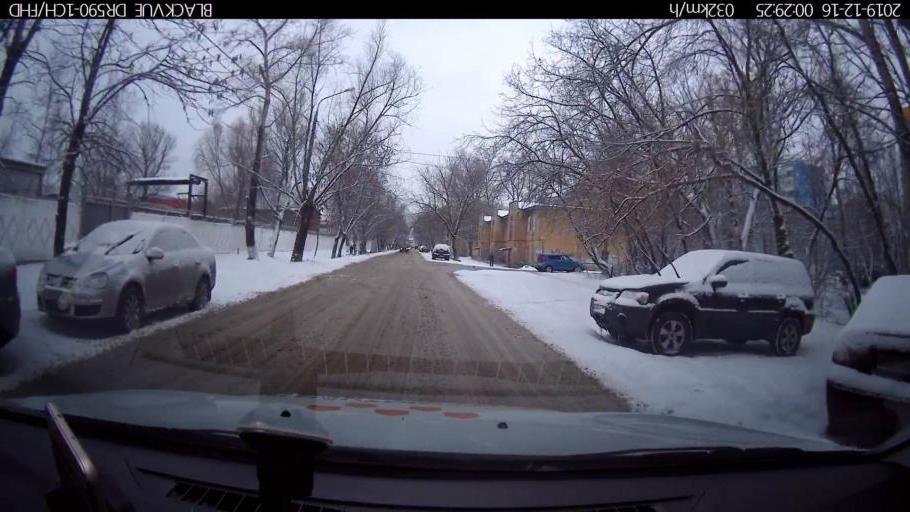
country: RU
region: Nizjnij Novgorod
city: Nizhniy Novgorod
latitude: 56.3127
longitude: 43.8903
